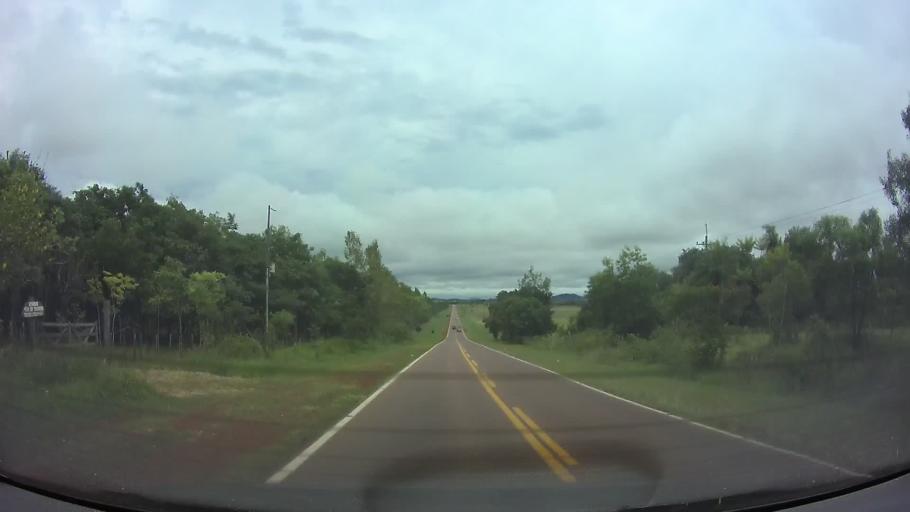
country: PY
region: Paraguari
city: Acahay
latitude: -25.8470
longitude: -57.1448
